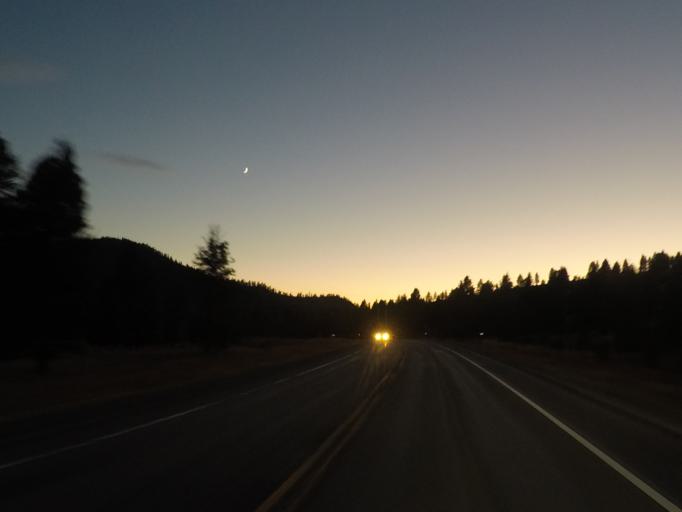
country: US
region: Montana
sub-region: Missoula County
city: Seeley Lake
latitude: 47.0289
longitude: -113.2832
